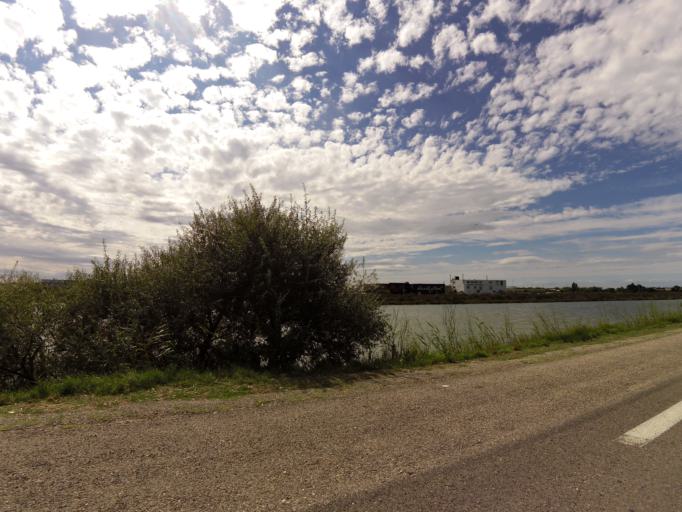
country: FR
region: Languedoc-Roussillon
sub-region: Departement du Gard
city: Le Grau-du-Roi
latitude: 43.5416
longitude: 4.1416
